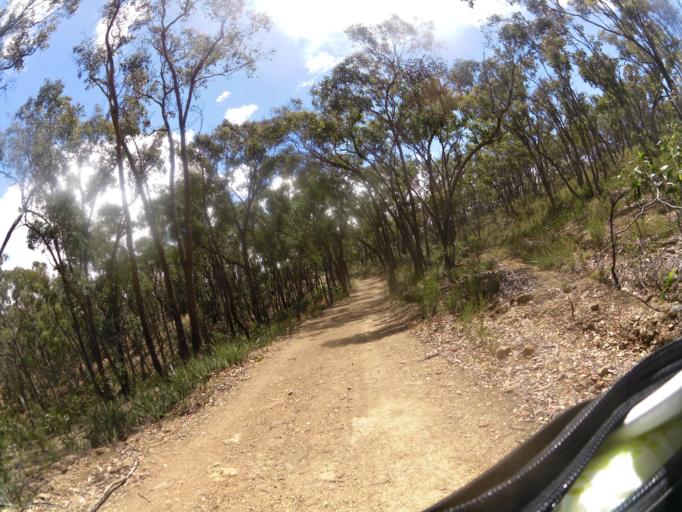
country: AU
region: Victoria
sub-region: Mount Alexander
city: Castlemaine
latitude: -37.0713
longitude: 144.2628
